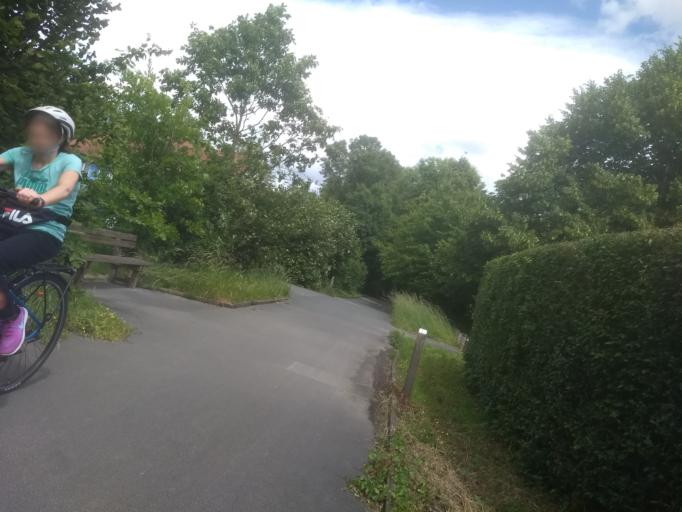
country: FR
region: Nord-Pas-de-Calais
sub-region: Departement du Pas-de-Calais
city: Beaumetz-les-Loges
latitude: 50.2366
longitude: 2.6545
